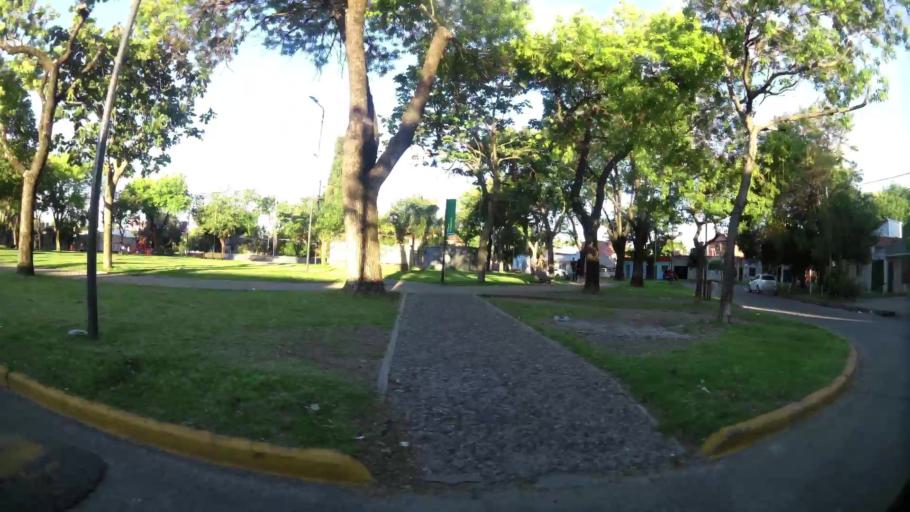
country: AR
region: Santa Fe
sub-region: Departamento de Rosario
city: Rosario
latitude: -32.9702
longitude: -60.6709
